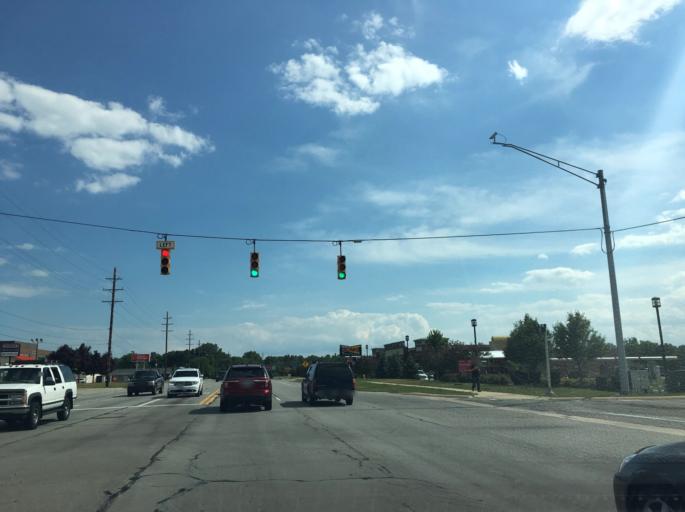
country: US
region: Michigan
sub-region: Macomb County
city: Clinton
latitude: 42.5956
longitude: -82.9004
